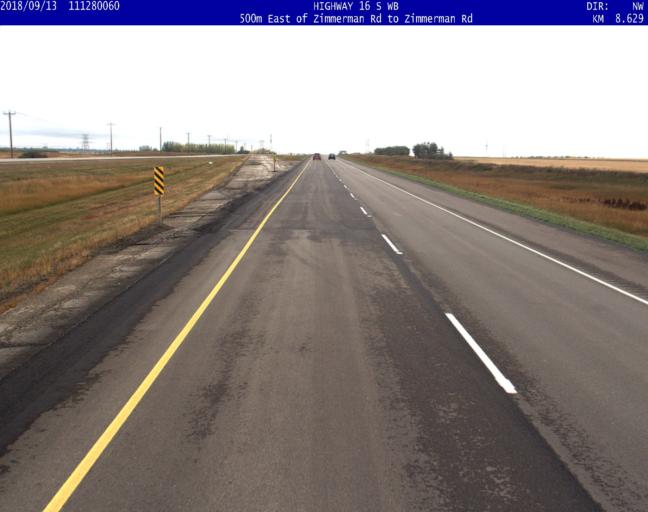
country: CA
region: Saskatchewan
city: Saskatoon
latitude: 52.0644
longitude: -106.4877
